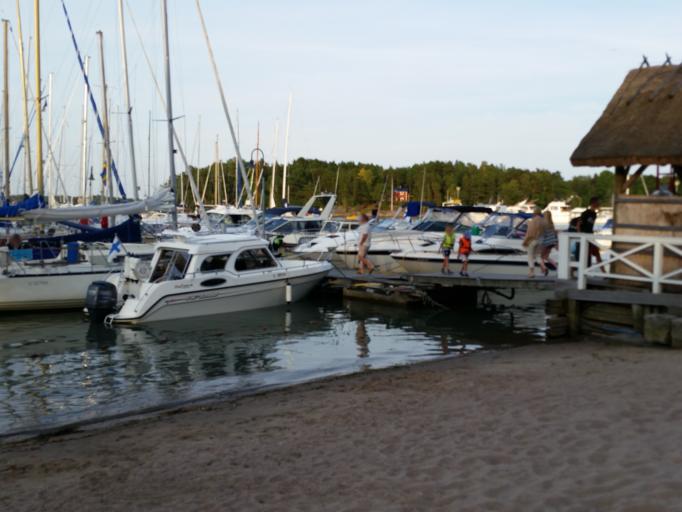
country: FI
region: Varsinais-Suomi
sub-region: Aboland-Turunmaa
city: Nagu
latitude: 60.1950
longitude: 21.9102
